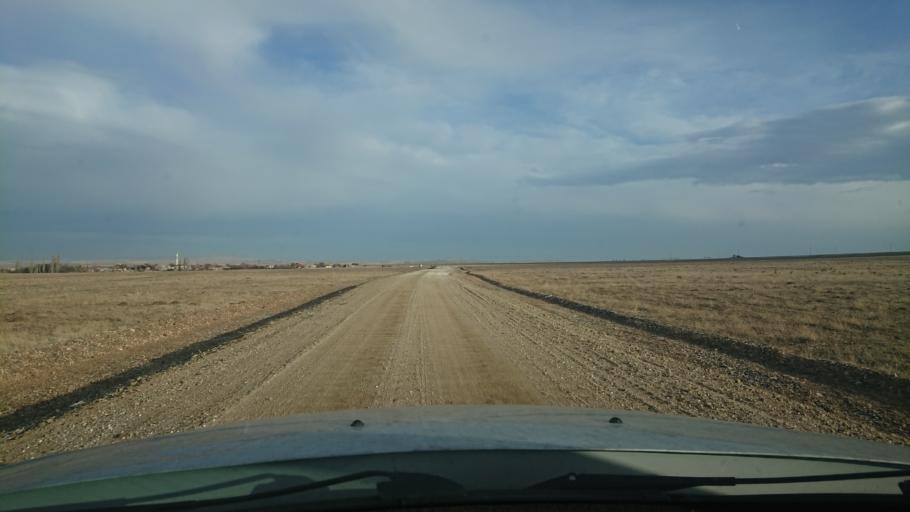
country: TR
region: Aksaray
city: Ortakoy
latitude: 38.7091
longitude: 33.8684
